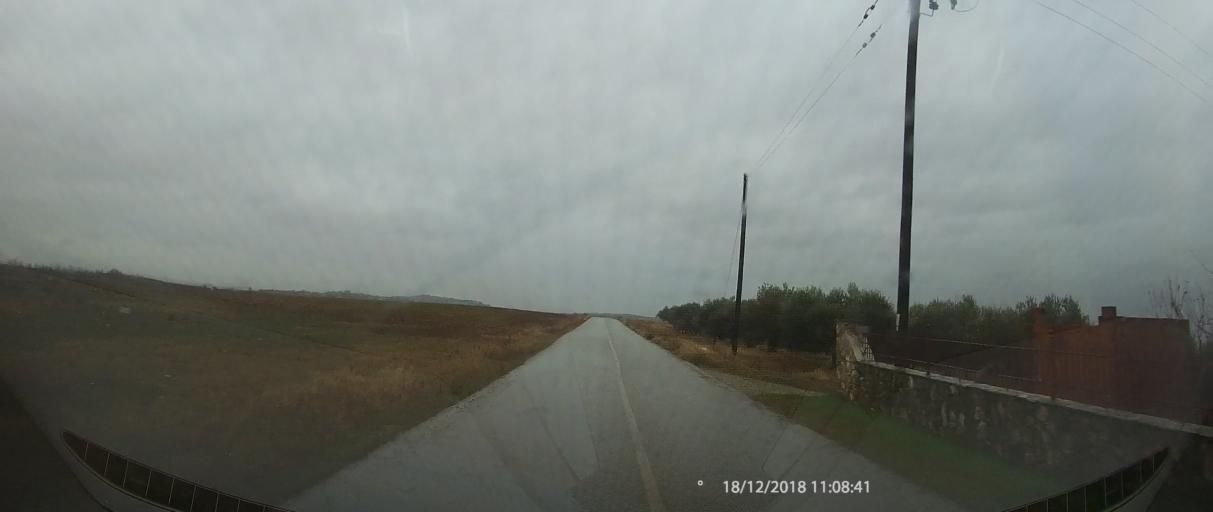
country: GR
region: Central Macedonia
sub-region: Nomos Pierias
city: Kato Milia
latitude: 40.2284
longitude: 22.3535
